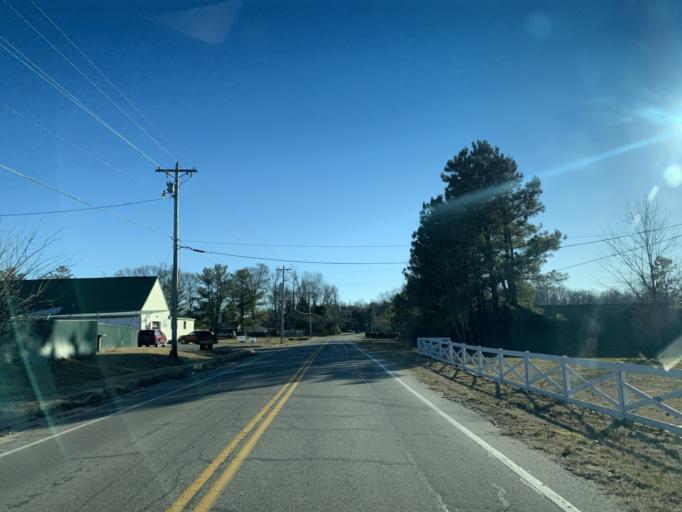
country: US
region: Maryland
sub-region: Saint Mary's County
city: Charlotte Hall
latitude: 38.4970
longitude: -76.7769
